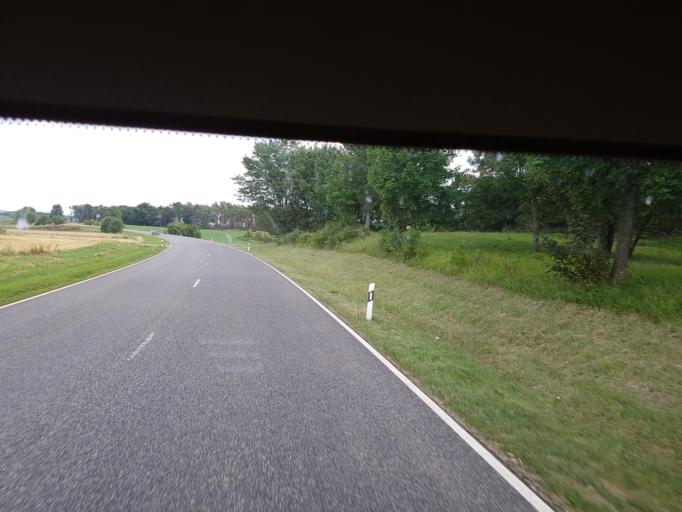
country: DE
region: Rheinland-Pfalz
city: Schwirzheim
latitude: 50.2178
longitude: 6.5244
